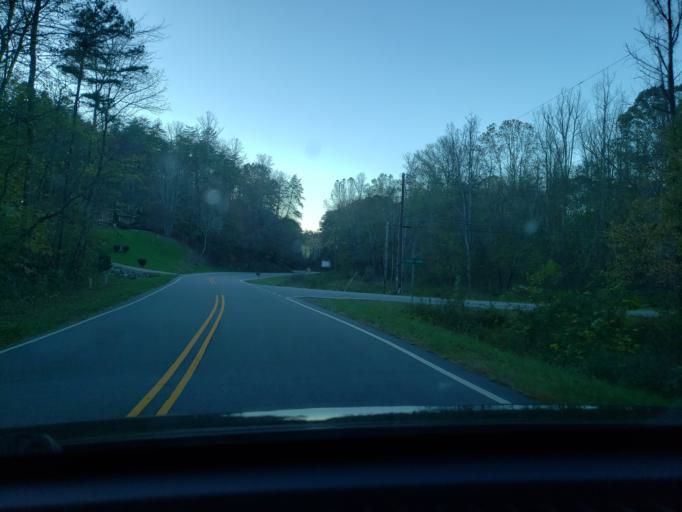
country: US
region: North Carolina
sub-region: Stokes County
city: Danbury
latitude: 36.3850
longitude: -80.1883
